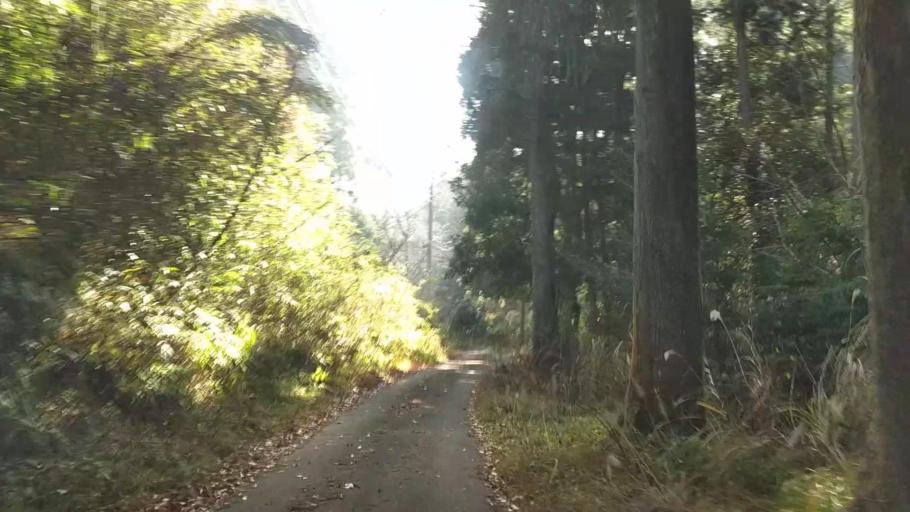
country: JP
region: Kanagawa
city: Isehara
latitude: 35.4433
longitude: 139.2872
